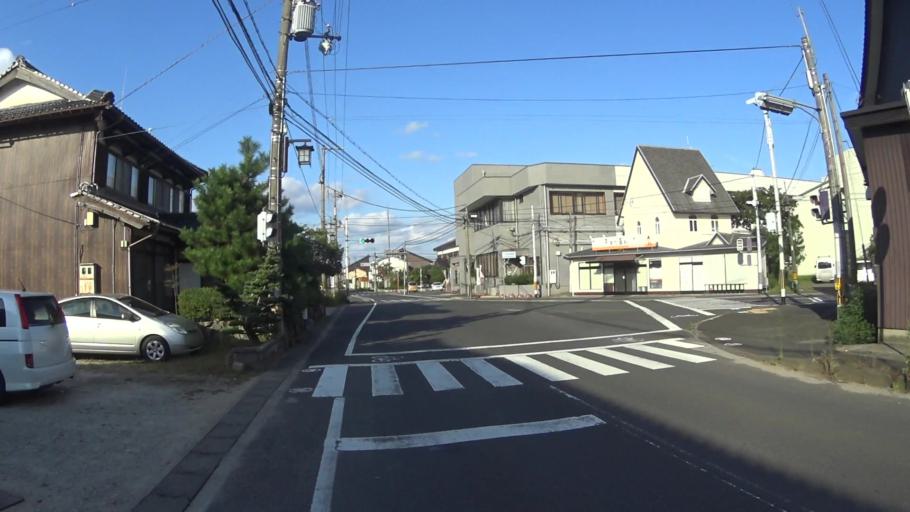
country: JP
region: Hyogo
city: Toyooka
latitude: 35.6031
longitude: 134.8942
